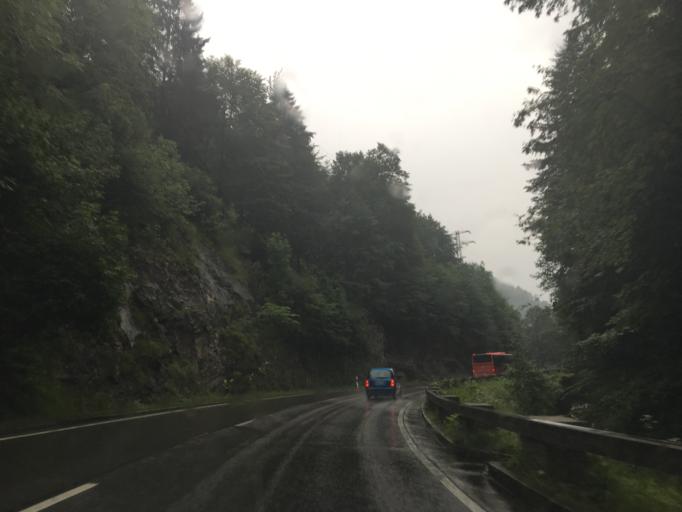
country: DE
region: Bavaria
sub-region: Upper Bavaria
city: Reit im Winkl
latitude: 47.7004
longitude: 12.4791
